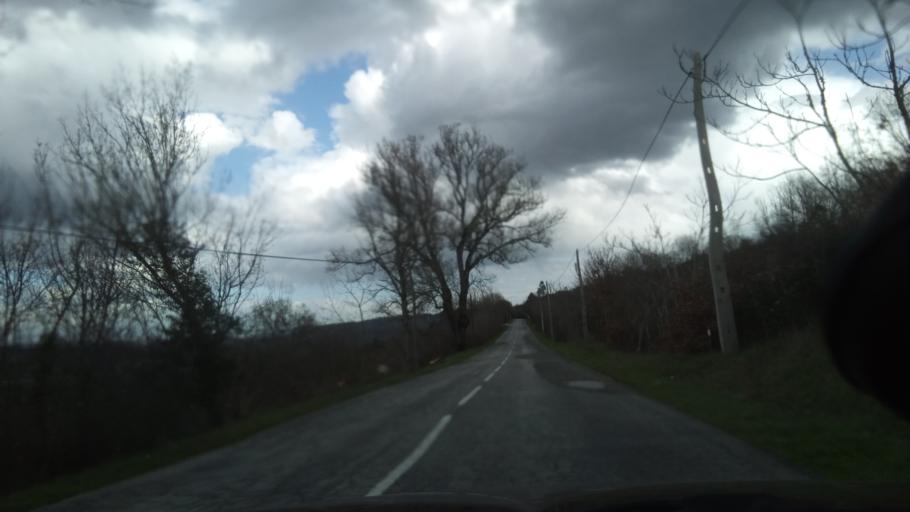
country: PT
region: Guarda
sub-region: Celorico da Beira
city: Celorico da Beira
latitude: 40.6277
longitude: -7.4545
